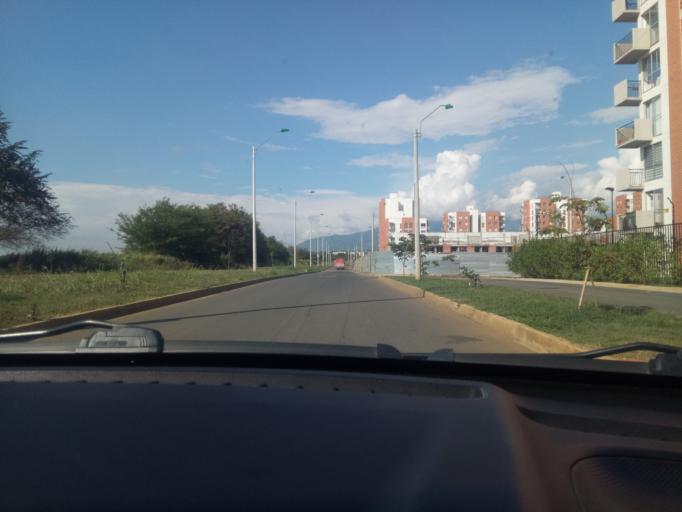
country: CO
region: Valle del Cauca
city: Cali
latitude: 3.3668
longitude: -76.5064
